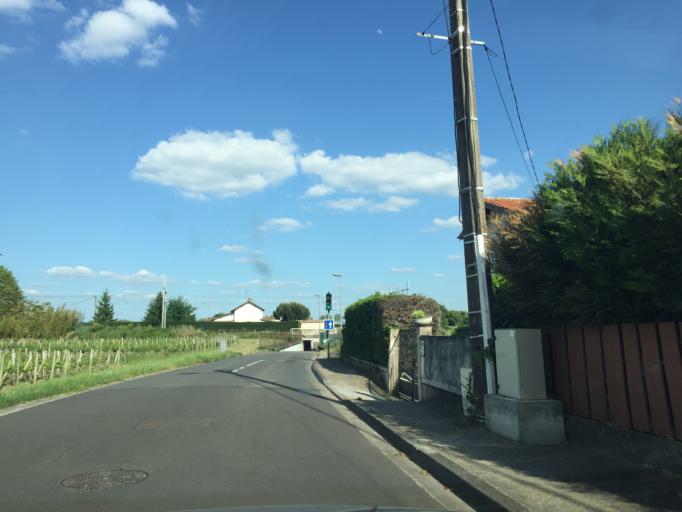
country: FR
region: Aquitaine
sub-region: Departement de la Gironde
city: Libourne
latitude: 44.9357
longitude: -0.2336
